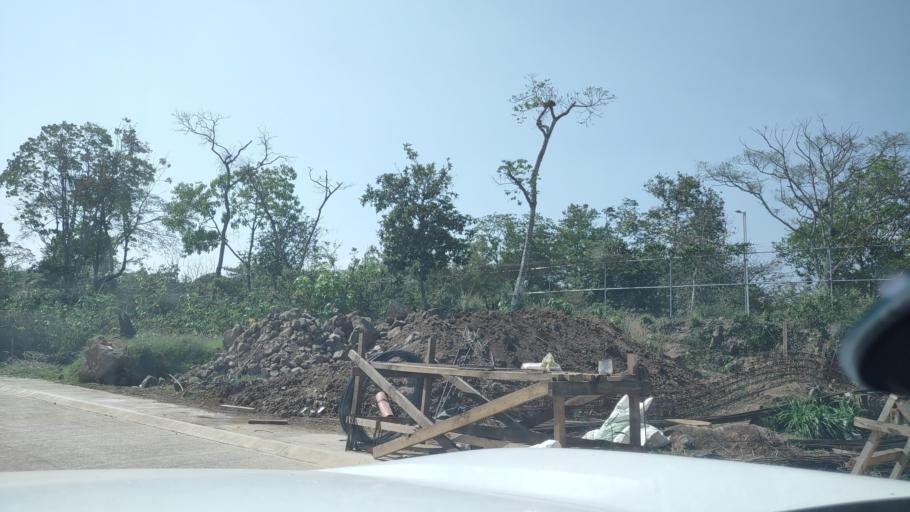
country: MX
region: Veracruz
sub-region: Emiliano Zapata
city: Las Trancas
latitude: 19.5246
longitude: -96.8696
